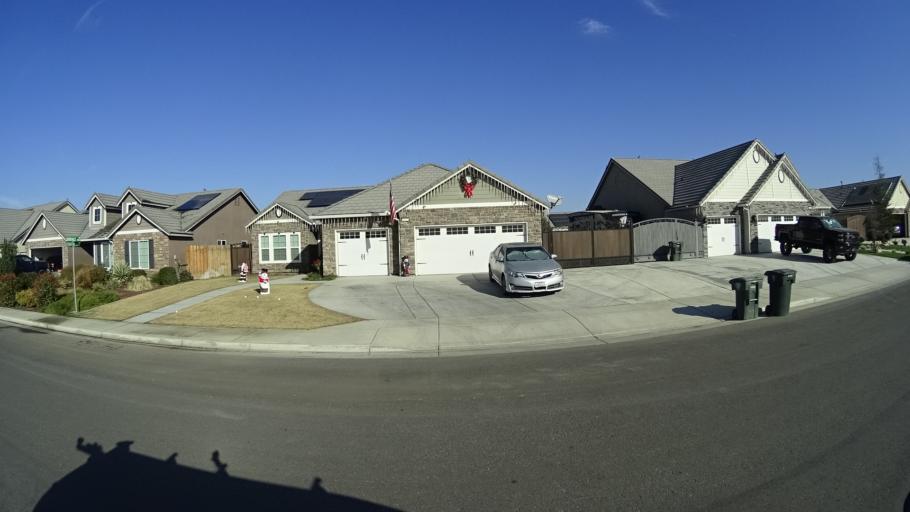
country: US
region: California
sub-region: Kern County
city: Greenfield
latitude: 35.2721
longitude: -119.0706
